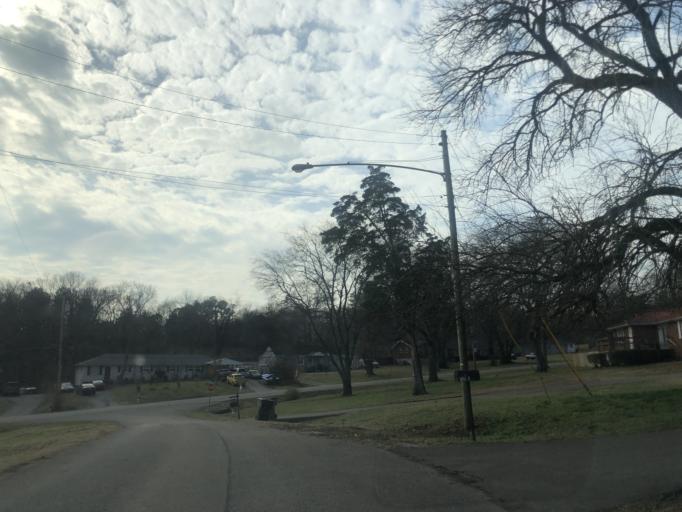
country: US
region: Tennessee
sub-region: Davidson County
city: Oak Hill
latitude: 36.1057
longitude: -86.7136
